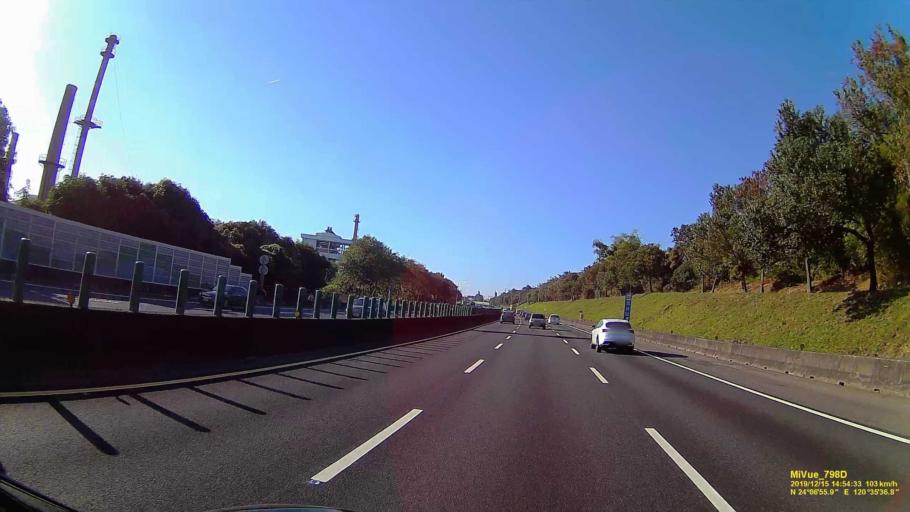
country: TW
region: Taiwan
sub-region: Changhua
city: Chang-hua
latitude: 24.1134
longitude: 120.5938
